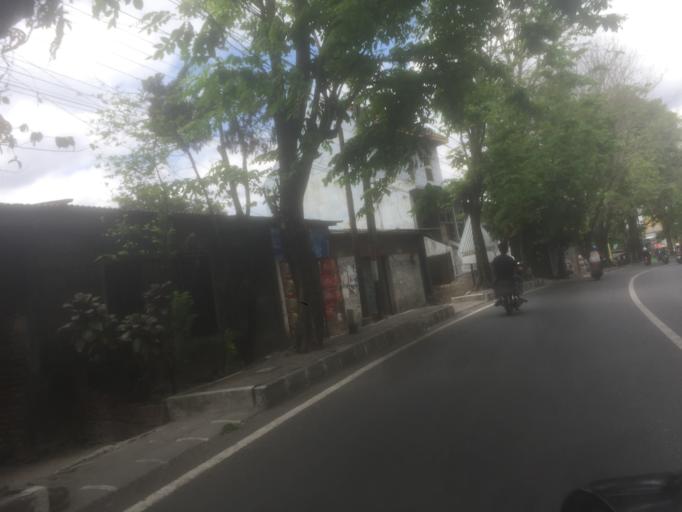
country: ID
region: Daerah Istimewa Yogyakarta
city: Melati
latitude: -7.7291
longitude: 110.3635
